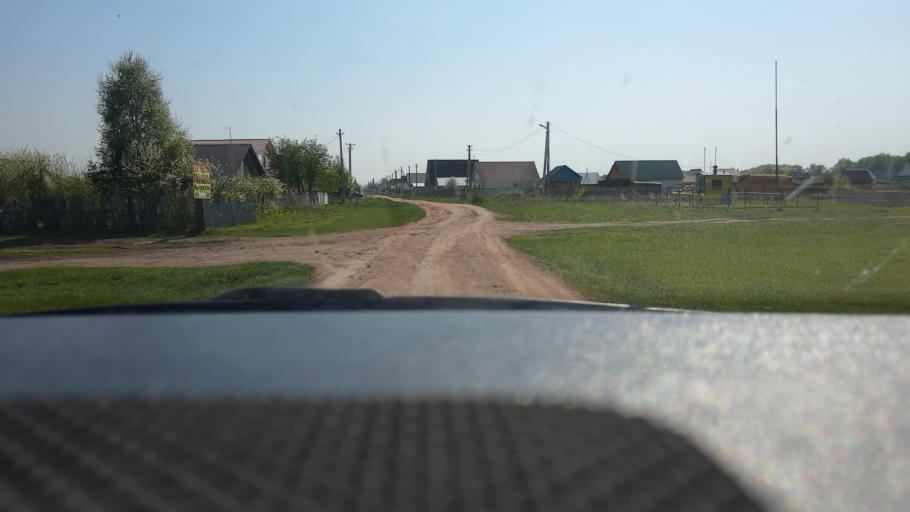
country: RU
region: Bashkortostan
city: Chishmy
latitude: 54.3971
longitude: 55.2132
